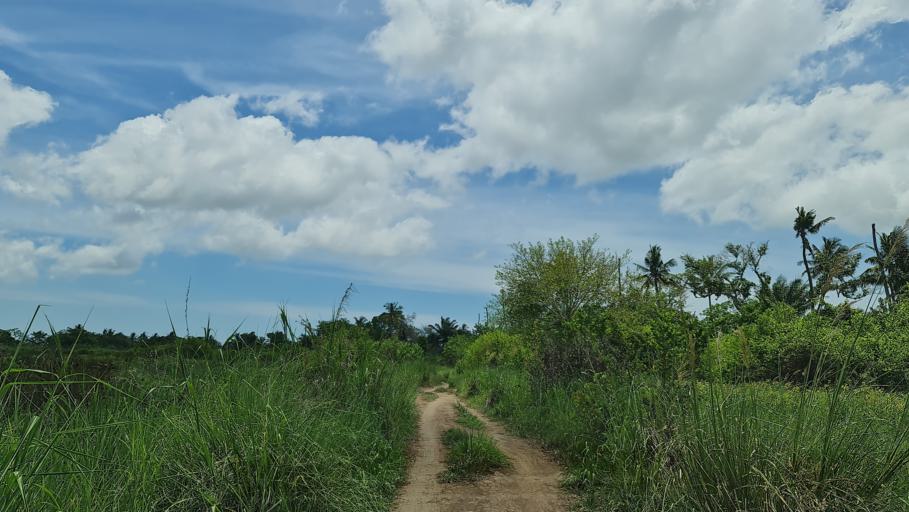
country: MZ
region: Zambezia
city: Quelimane
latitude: -17.5850
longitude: 37.3872
